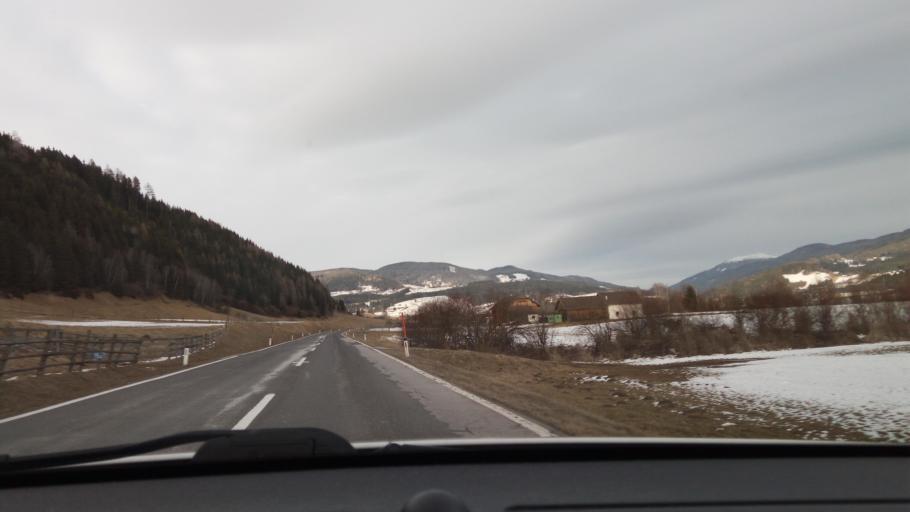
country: AT
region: Salzburg
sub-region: Politischer Bezirk Tamsweg
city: Sankt Andra im Lungau
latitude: 47.1251
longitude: 13.7755
